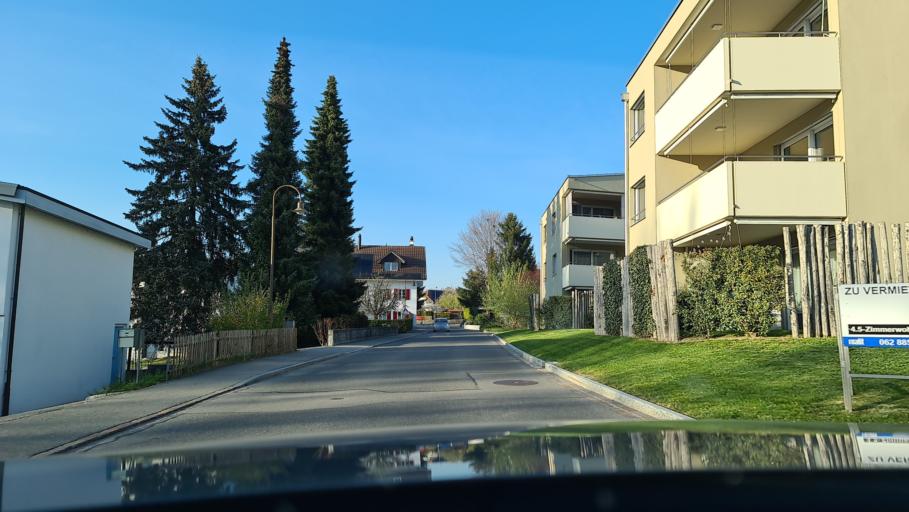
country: CH
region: Aargau
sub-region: Bezirk Lenzburg
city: Seon
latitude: 47.3458
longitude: 8.1634
